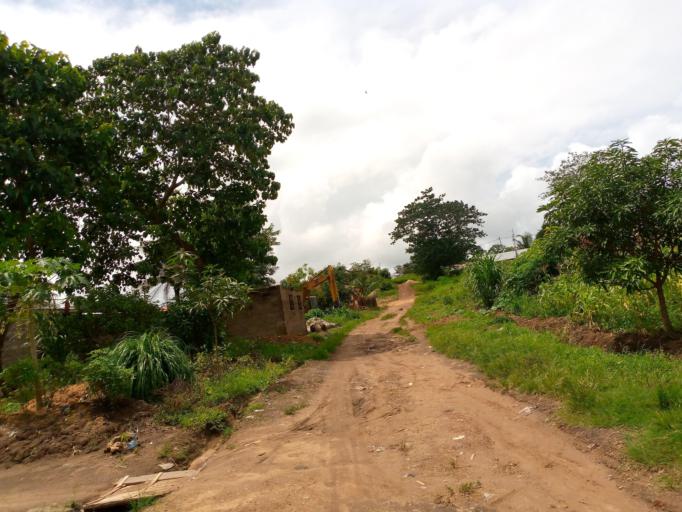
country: SL
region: Northern Province
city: Magburaka
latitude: 8.7281
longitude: -11.9366
